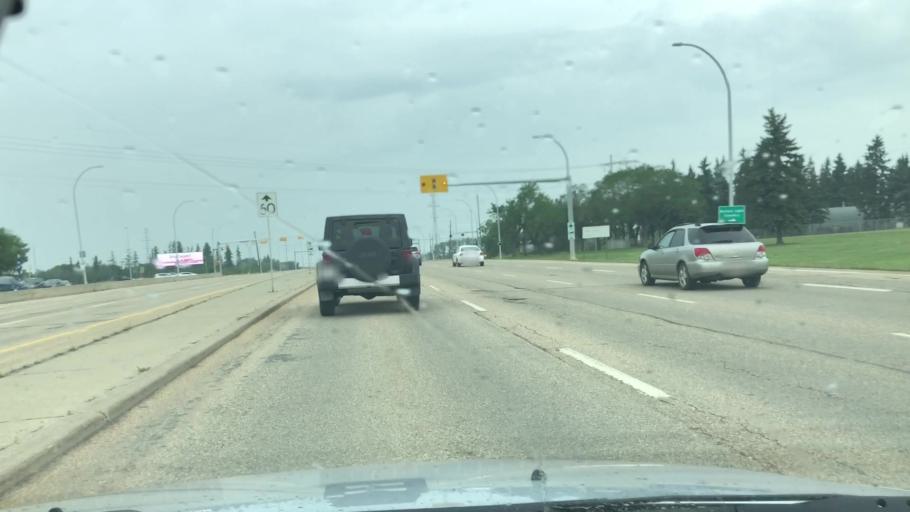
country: CA
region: Alberta
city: St. Albert
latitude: 53.6105
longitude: -113.5891
